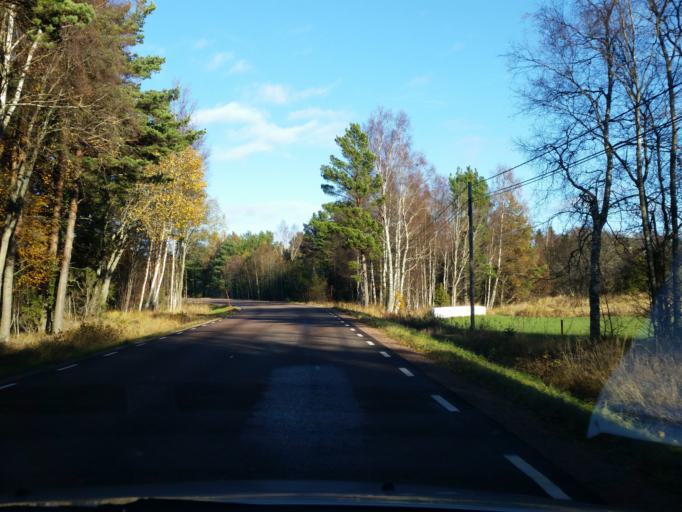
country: AX
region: Mariehamns stad
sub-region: Mariehamn
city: Mariehamn
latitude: 60.1390
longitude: 19.8586
